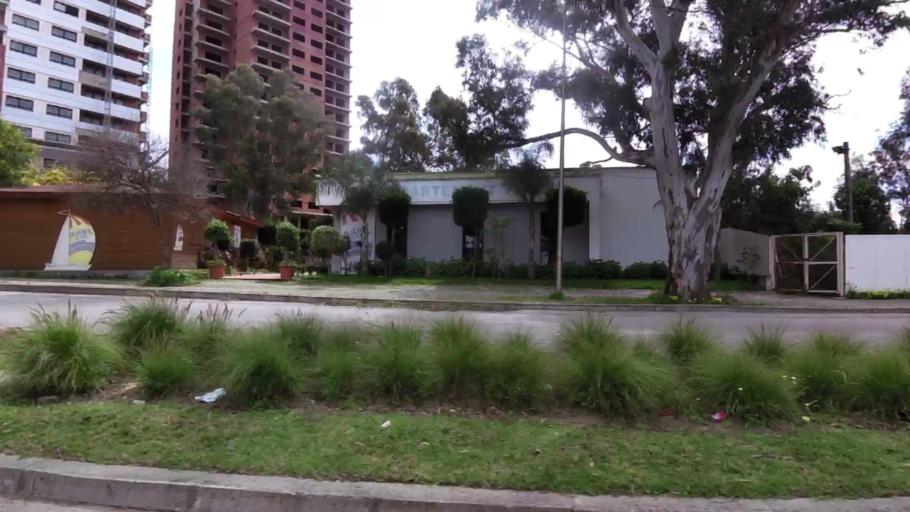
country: MA
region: Tanger-Tetouan
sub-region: Tanger-Assilah
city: Tangier
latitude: 35.7731
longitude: -5.7779
